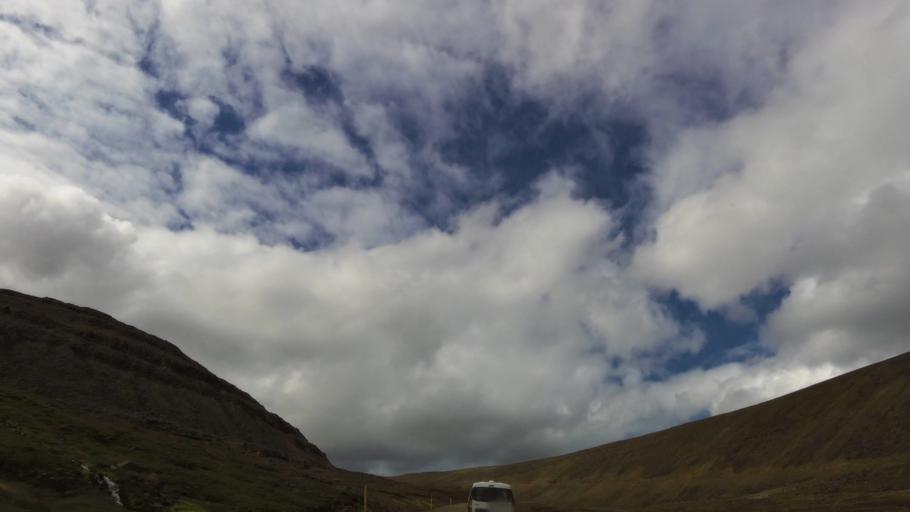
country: IS
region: Westfjords
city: Isafjoerdur
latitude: 66.1699
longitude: -23.3498
